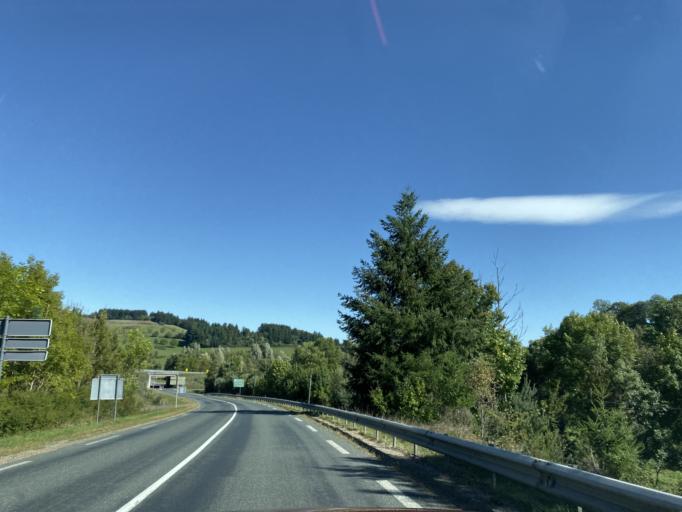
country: FR
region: Rhone-Alpes
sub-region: Departement de la Loire
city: Saint-Just-en-Chevalet
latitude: 45.8681
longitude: 3.8290
